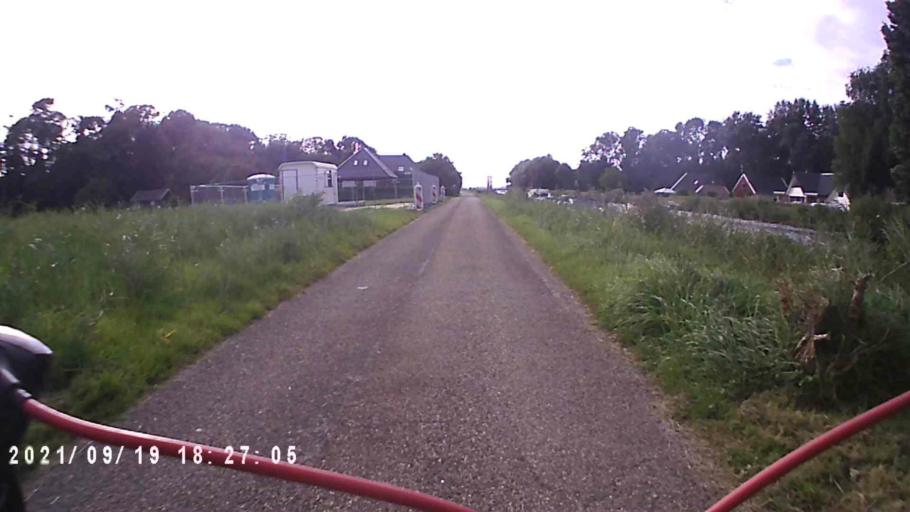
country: NL
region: Groningen
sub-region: Gemeente Appingedam
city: Appingedam
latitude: 53.2736
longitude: 6.8461
